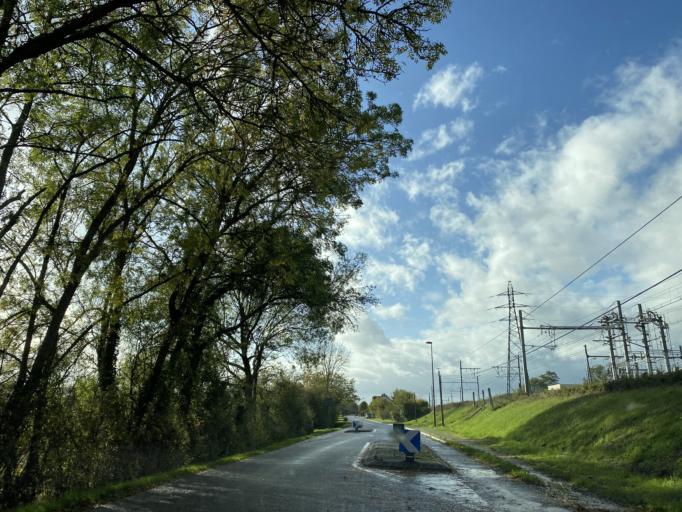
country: FR
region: Centre
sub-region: Departement du Cher
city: Saint-Doulchard
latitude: 47.0945
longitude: 2.3690
